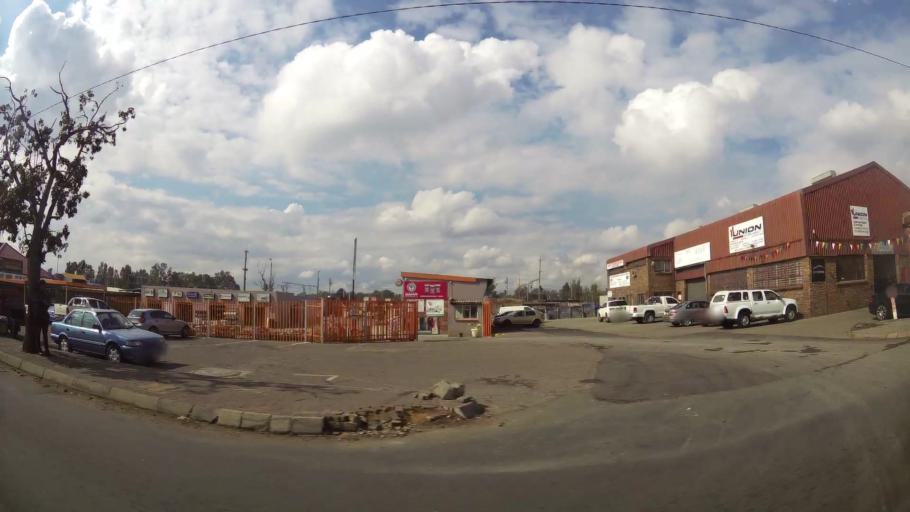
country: ZA
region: Gauteng
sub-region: Sedibeng District Municipality
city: Vereeniging
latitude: -26.6699
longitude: 27.9350
